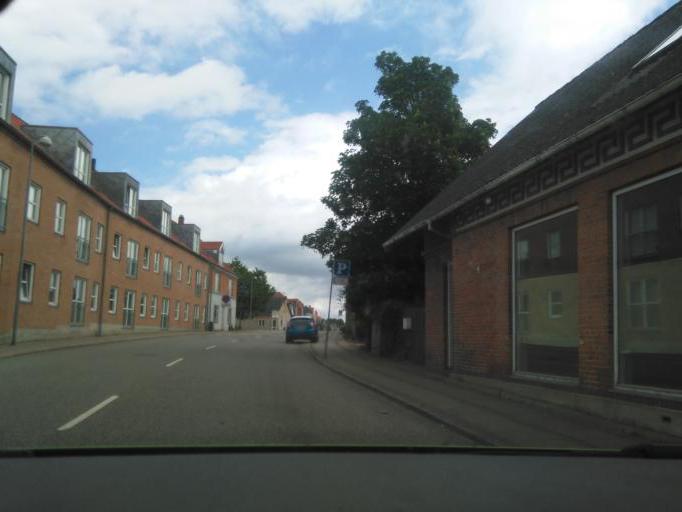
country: DK
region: Zealand
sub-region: Kalundborg Kommune
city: Gorlev
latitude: 55.5393
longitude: 11.2292
